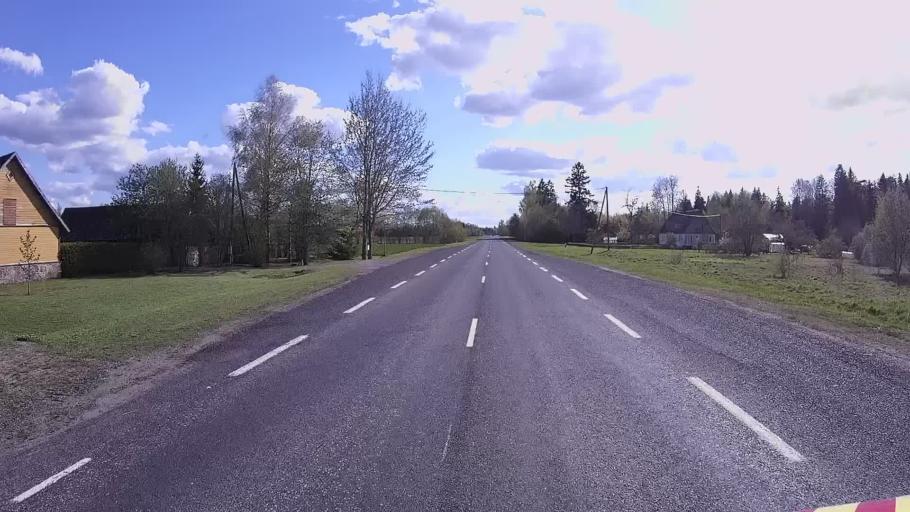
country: EE
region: Jogevamaa
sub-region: Jogeva linn
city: Jogeva
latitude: 58.7182
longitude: 26.1848
